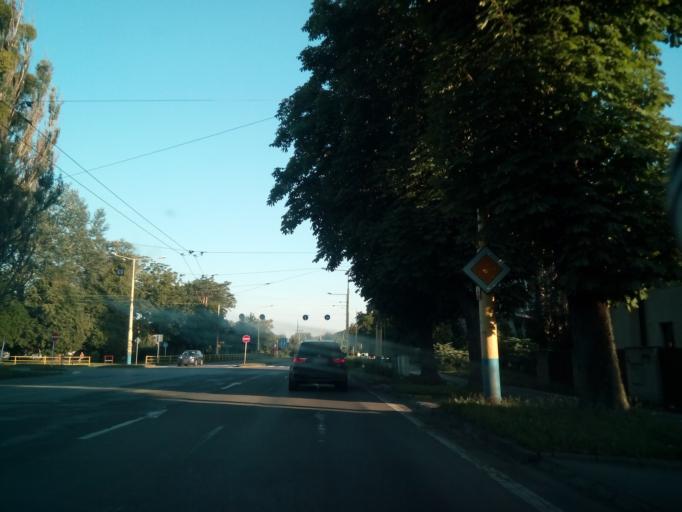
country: SK
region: Presovsky
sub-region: Okres Presov
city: Presov
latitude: 48.9946
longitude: 21.2297
